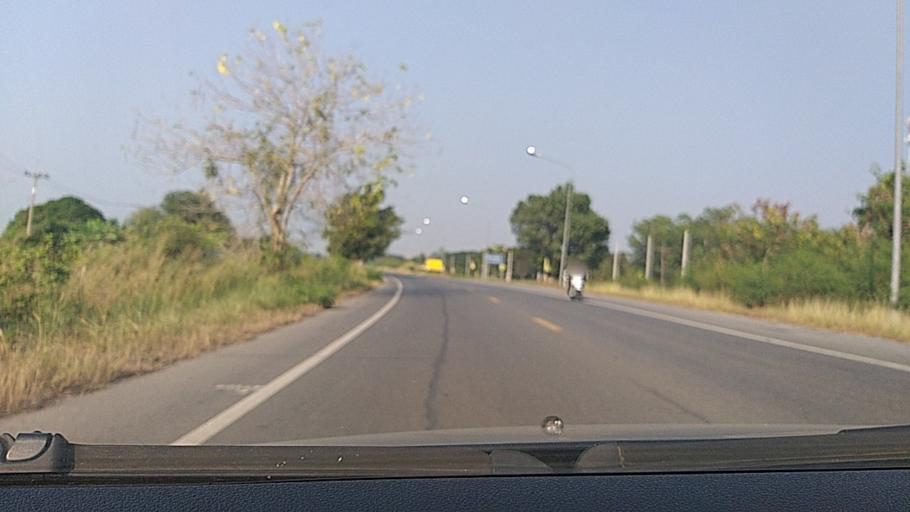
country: TH
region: Sing Buri
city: Tha Chang
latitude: 14.7363
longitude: 100.4354
